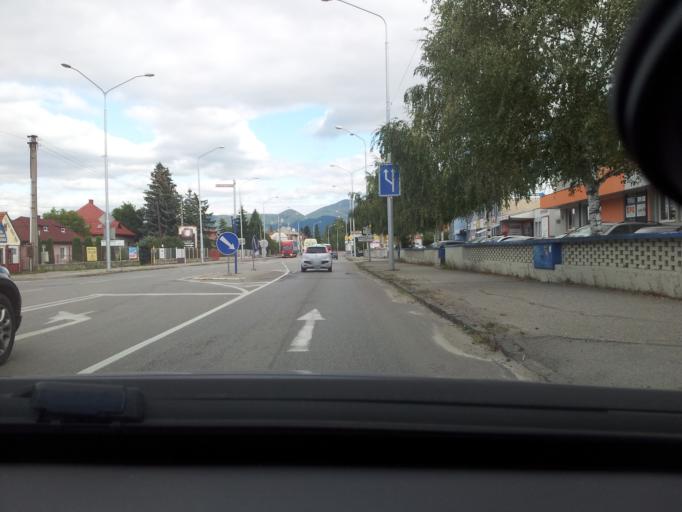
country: SK
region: Zilinsky
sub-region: Okres Martin
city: Martin
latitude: 49.0521
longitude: 18.9146
